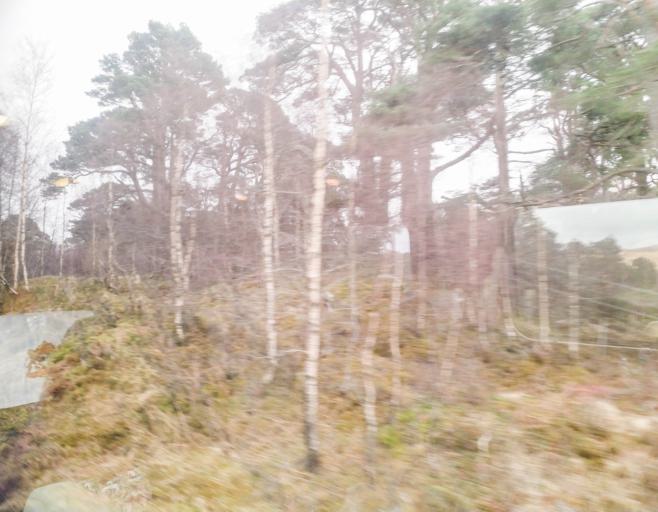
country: GB
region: Scotland
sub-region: Highland
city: Spean Bridge
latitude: 56.5797
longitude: -4.6775
